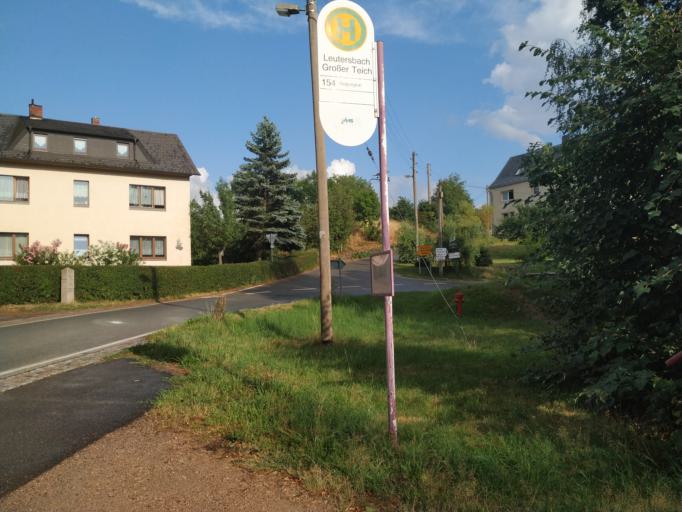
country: DE
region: Saxony
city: Kirchberg
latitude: 50.5959
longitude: 12.5228
